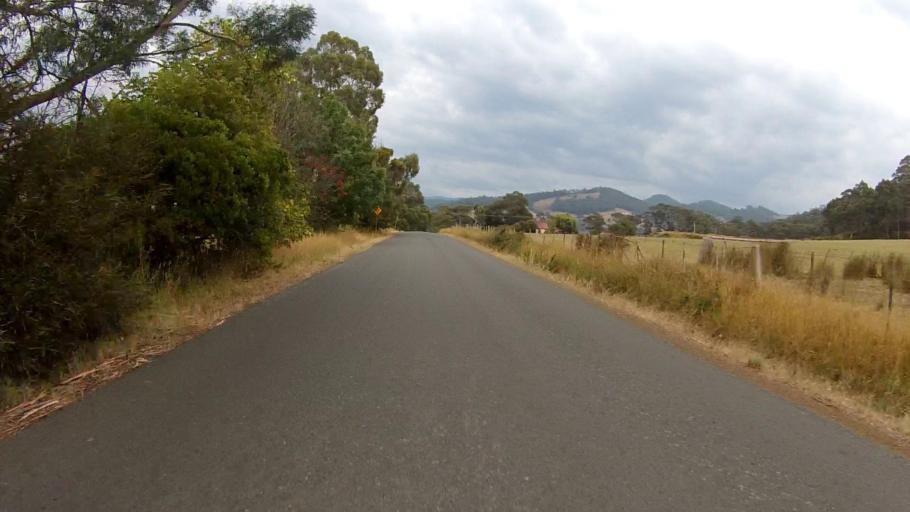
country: AU
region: Tasmania
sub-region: Huon Valley
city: Cygnet
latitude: -43.1837
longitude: 147.1094
